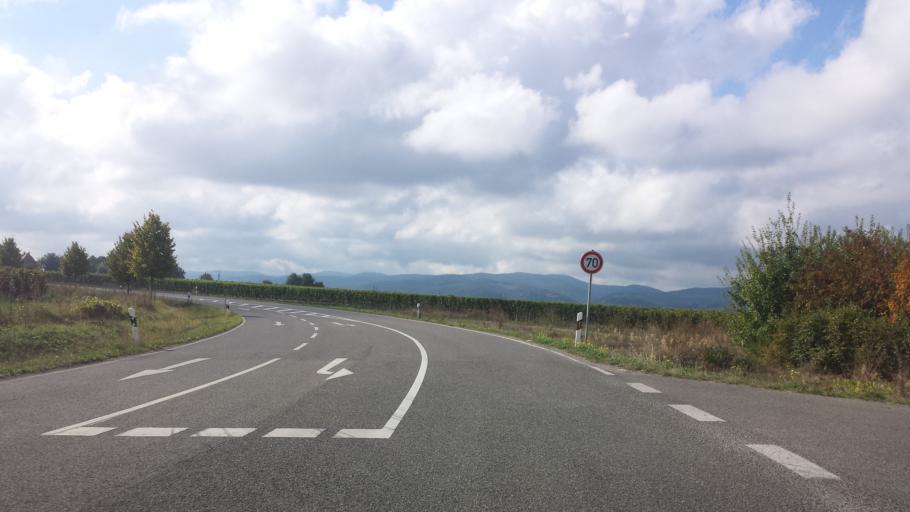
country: DE
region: Rheinland-Pfalz
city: Friedelsheim
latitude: 49.4620
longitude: 8.2279
